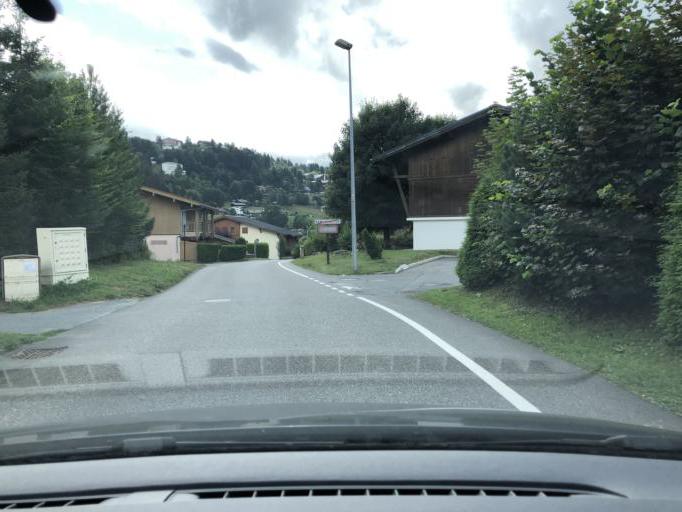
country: FR
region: Rhone-Alpes
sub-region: Departement de la Haute-Savoie
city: Megeve
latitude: 45.8683
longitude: 6.6238
